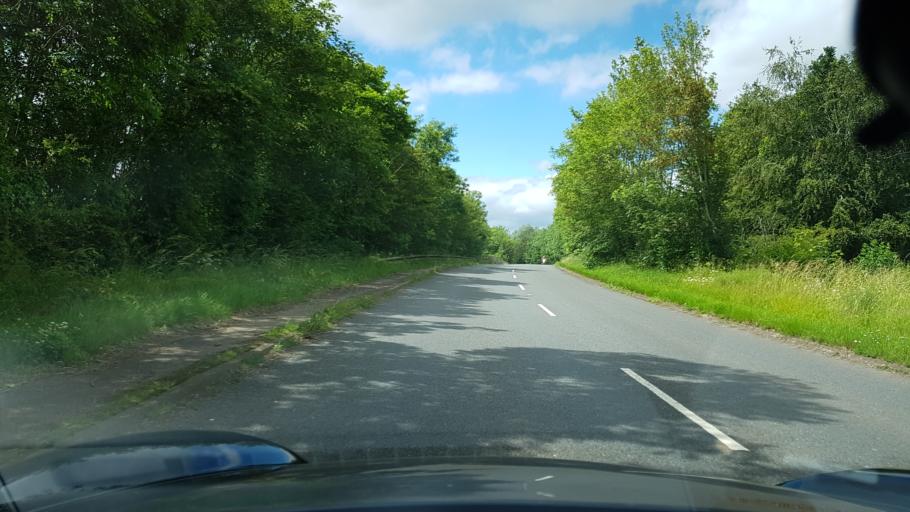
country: GB
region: Wales
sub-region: Monmouthshire
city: Llanarth
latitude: 51.7831
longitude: -2.9519
